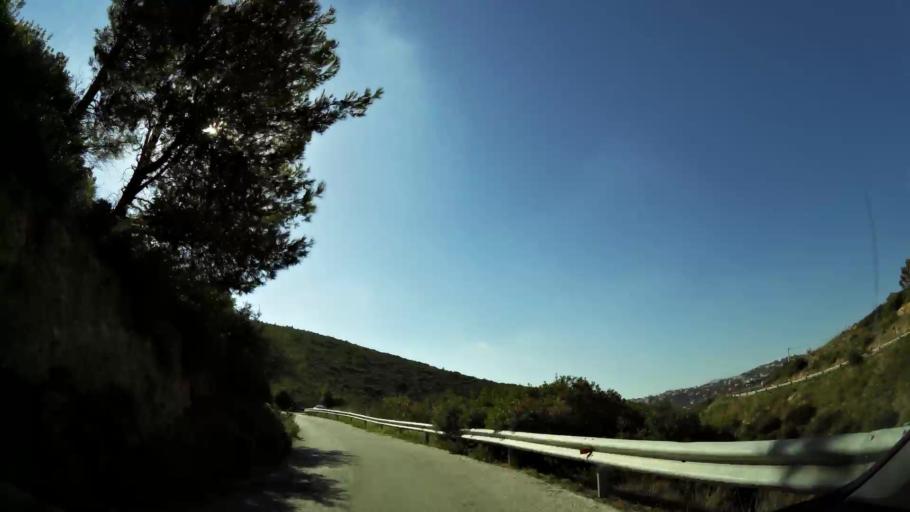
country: GR
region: Attica
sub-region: Nomarchia Anatolikis Attikis
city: Dhrafi
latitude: 38.0432
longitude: 23.9104
